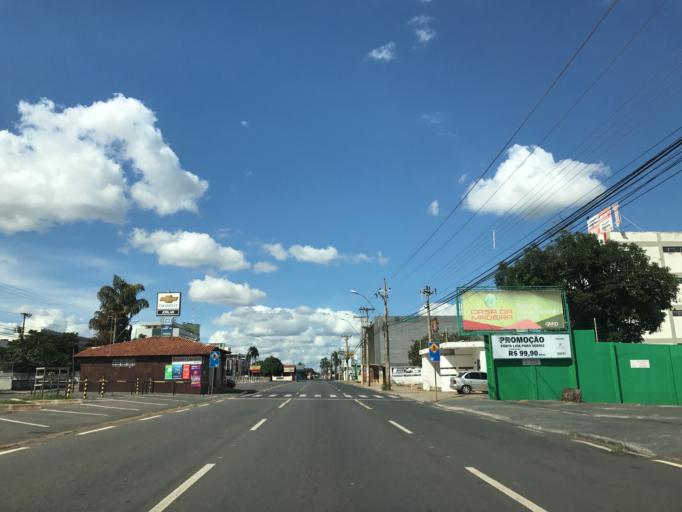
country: BR
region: Federal District
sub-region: Brasilia
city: Brasilia
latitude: -15.8035
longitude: -47.9631
